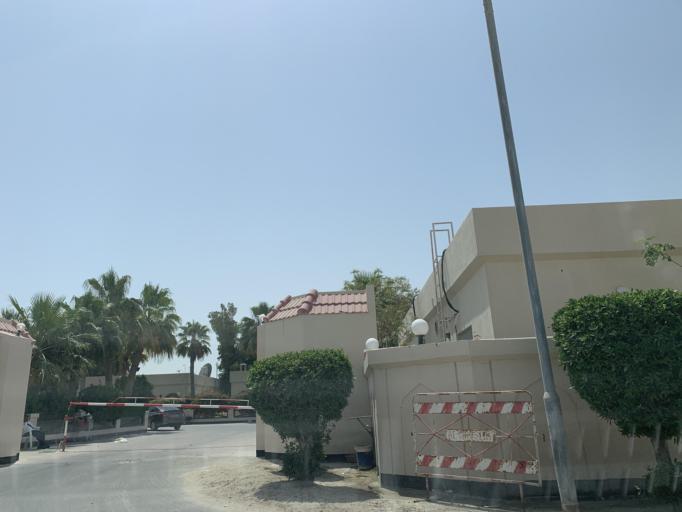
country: BH
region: Manama
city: Jidd Hafs
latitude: 26.1978
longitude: 50.5630
